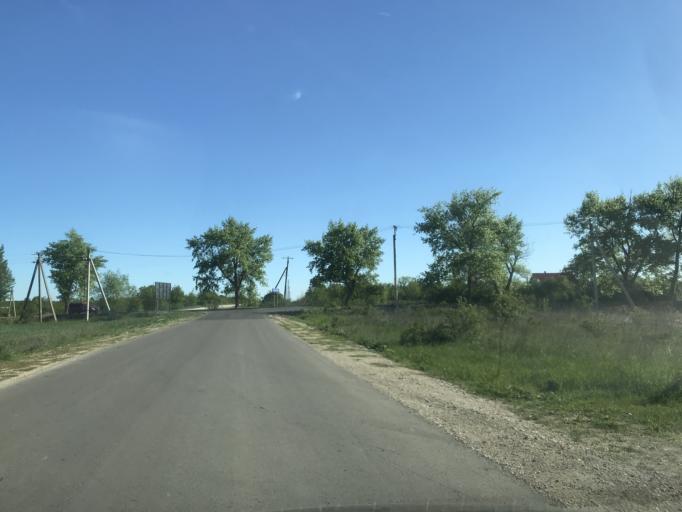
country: MD
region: Chisinau
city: Cricova
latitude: 47.2486
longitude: 28.8173
